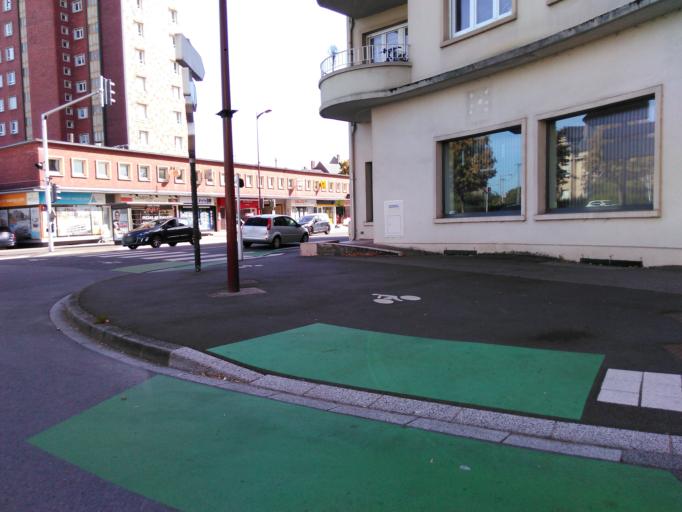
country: FR
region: Lorraine
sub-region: Departement de la Moselle
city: Thionville
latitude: 49.3632
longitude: 6.1692
